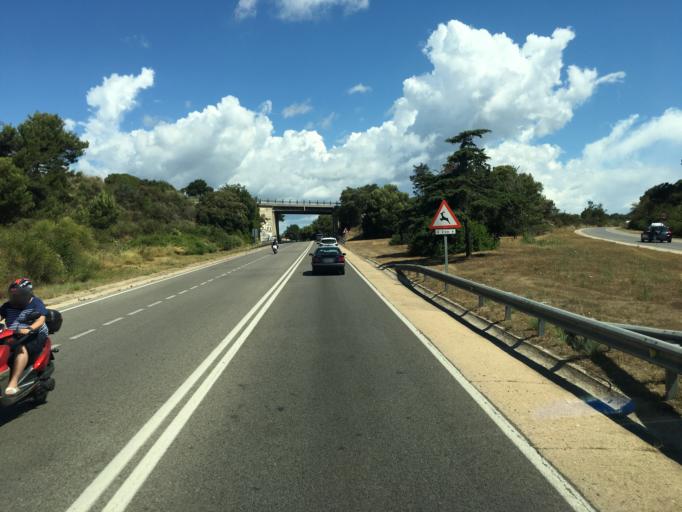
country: ES
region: Catalonia
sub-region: Provincia de Barcelona
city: Malgrat de Mar
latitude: 41.6533
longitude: 2.7351
